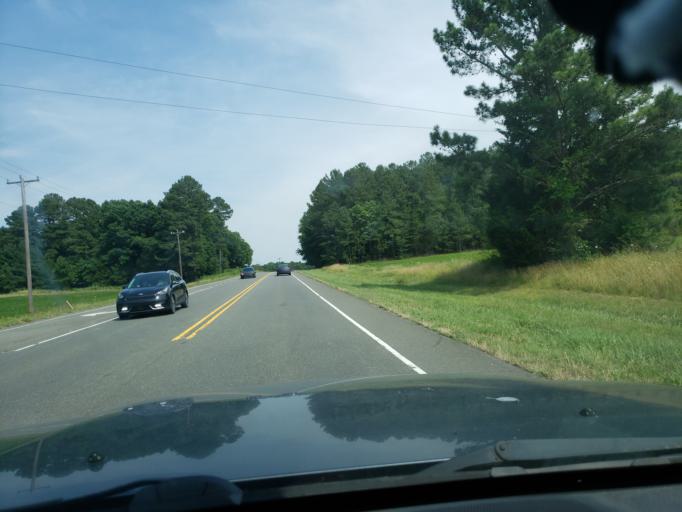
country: US
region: North Carolina
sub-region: Alamance County
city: Saxapahaw
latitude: 35.9395
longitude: -79.2389
